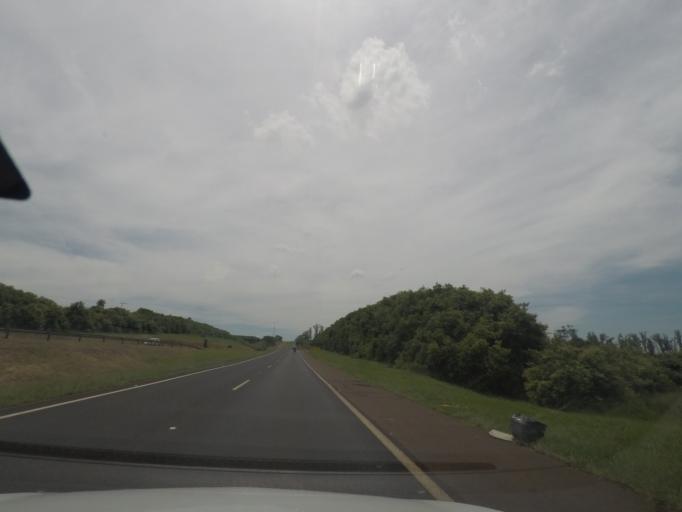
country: BR
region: Sao Paulo
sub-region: Bebedouro
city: Bebedouro
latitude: -21.0019
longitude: -48.4300
